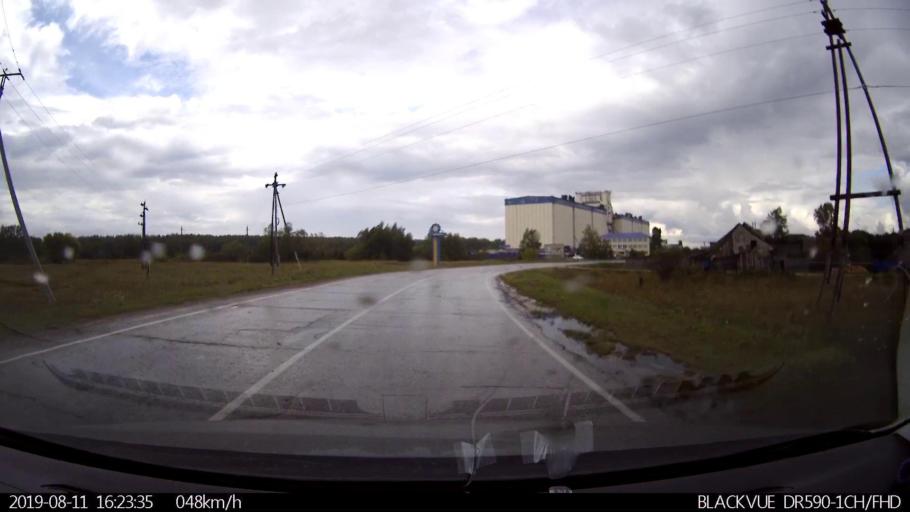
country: RU
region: Ulyanovsk
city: Mayna
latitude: 54.0960
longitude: 47.5883
